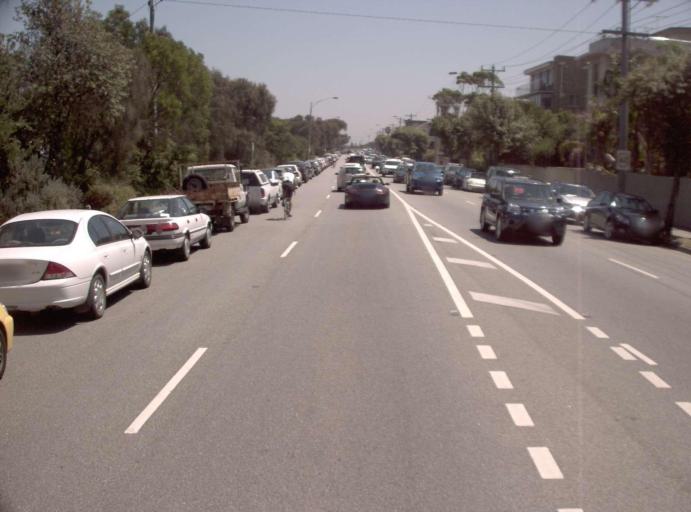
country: AU
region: Victoria
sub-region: Port Phillip
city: Elwood
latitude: -37.8872
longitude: 144.9841
